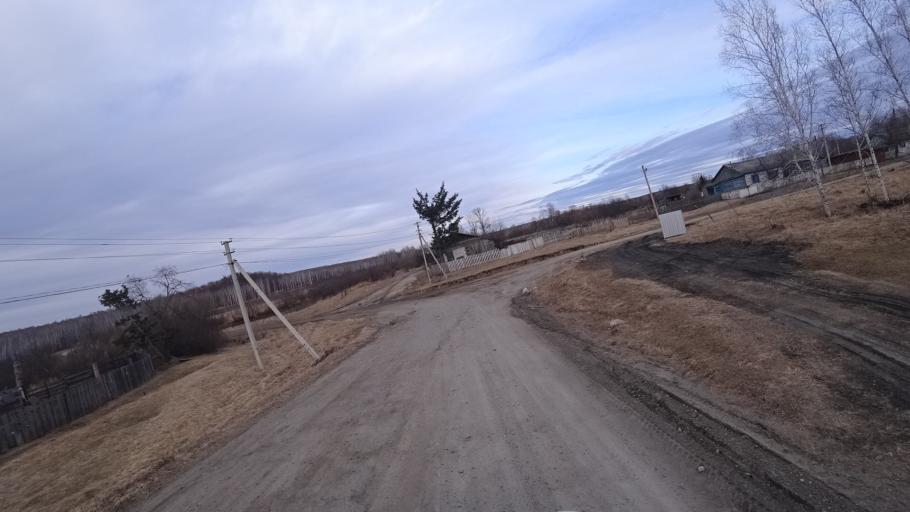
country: RU
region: Amur
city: Bureya
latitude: 50.0211
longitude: 129.7773
